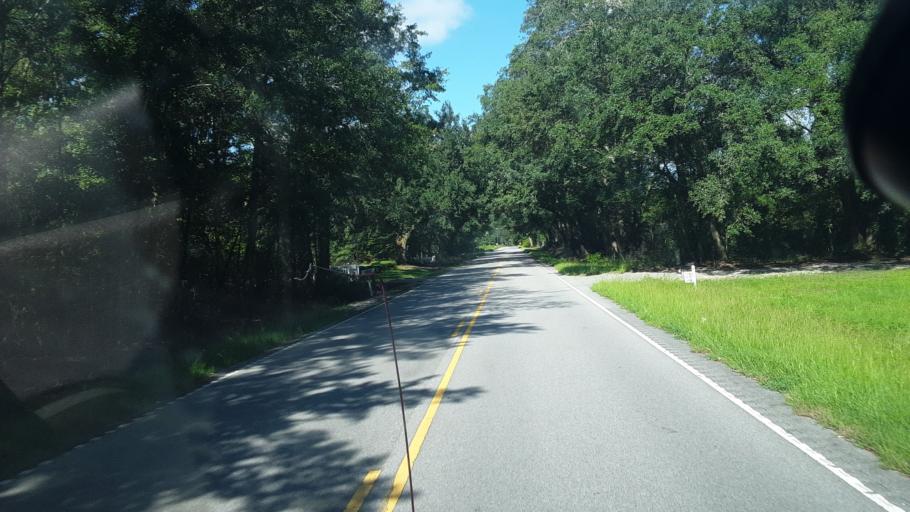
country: US
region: South Carolina
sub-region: Jasper County
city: Ridgeland
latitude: 32.5913
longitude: -80.9737
